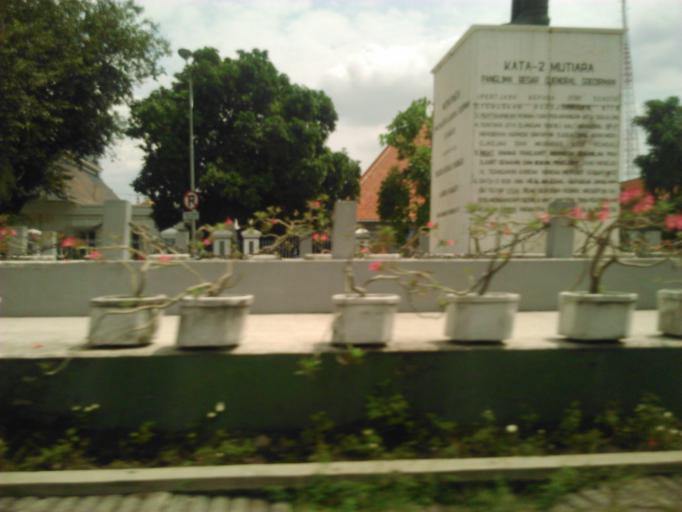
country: ID
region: East Java
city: Pacarkeling
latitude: -7.2617
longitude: 112.7465
